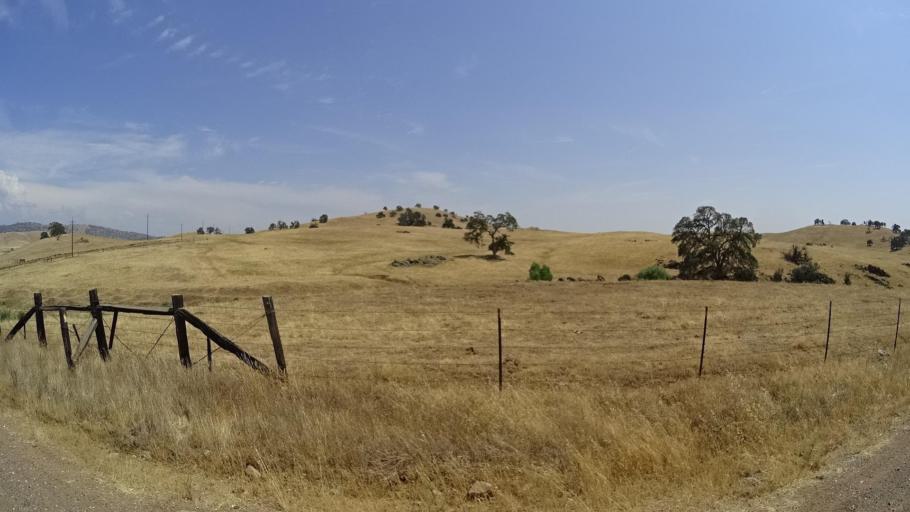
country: US
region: California
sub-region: Mariposa County
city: Mariposa
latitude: 37.5246
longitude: -120.2142
